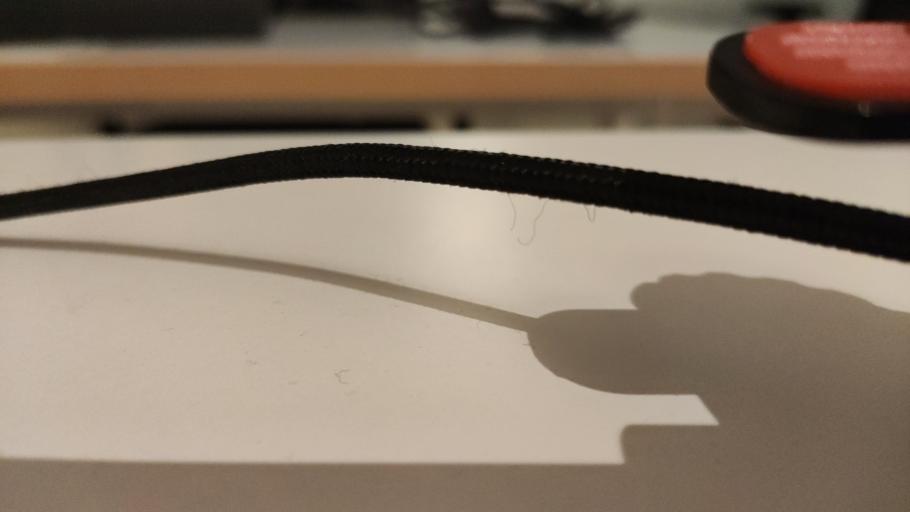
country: RU
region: Moskovskaya
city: Kurovskoye
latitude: 55.5877
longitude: 38.9056
